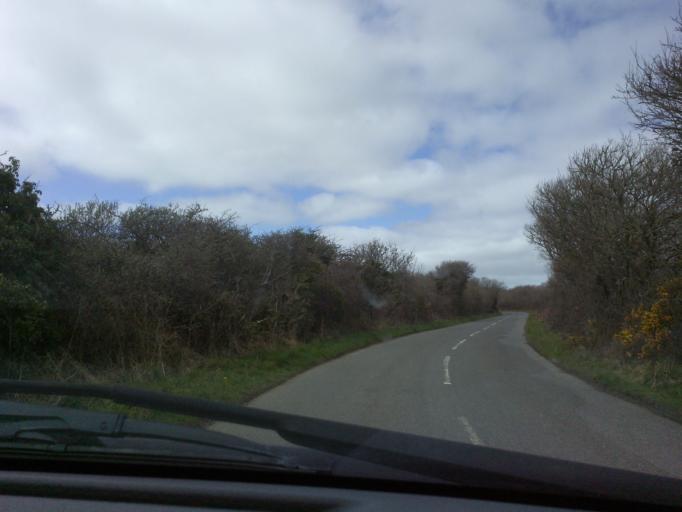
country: GB
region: England
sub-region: Cornwall
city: St. Buryan
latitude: 50.0594
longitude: -5.6258
